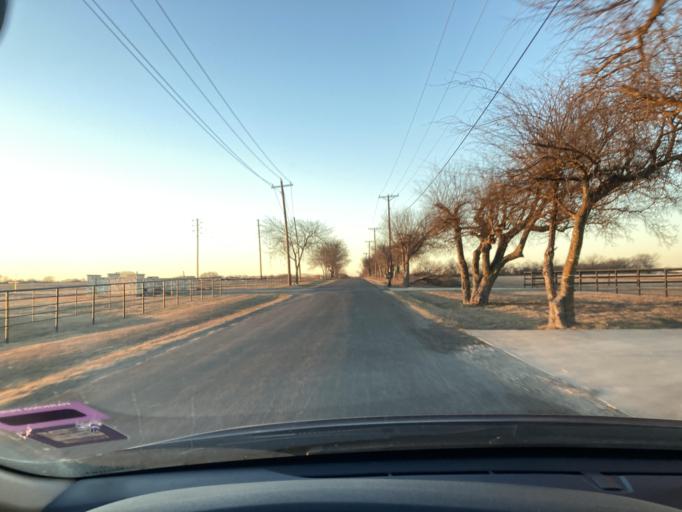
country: US
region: Texas
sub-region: Ellis County
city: Nash
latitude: 32.2865
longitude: -96.9072
